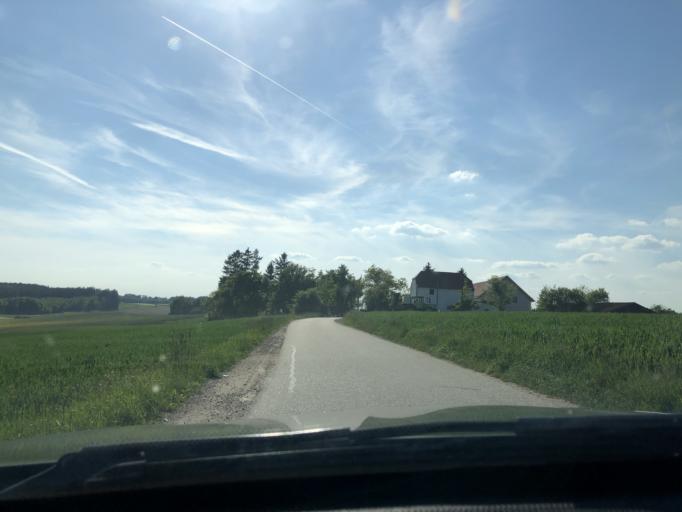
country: DE
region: Bavaria
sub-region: Upper Bavaria
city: Wolfersdorf
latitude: 48.4353
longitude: 11.7065
